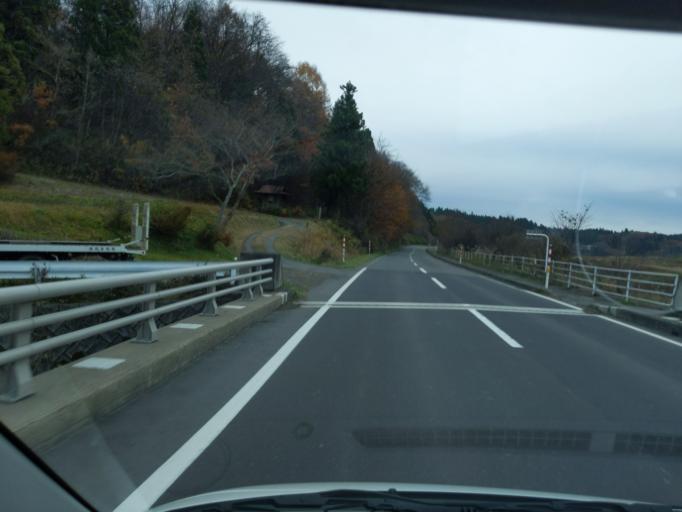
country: JP
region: Iwate
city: Kitakami
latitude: 39.2687
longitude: 141.2678
